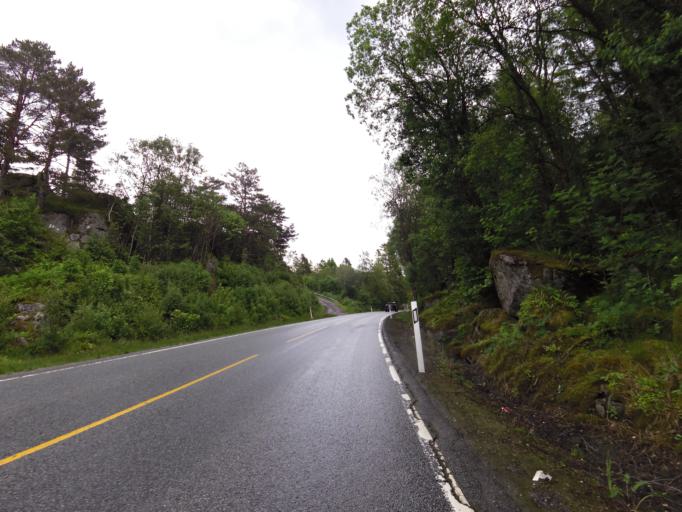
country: NO
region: Vest-Agder
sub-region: Farsund
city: Farsund
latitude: 58.1004
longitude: 6.8393
